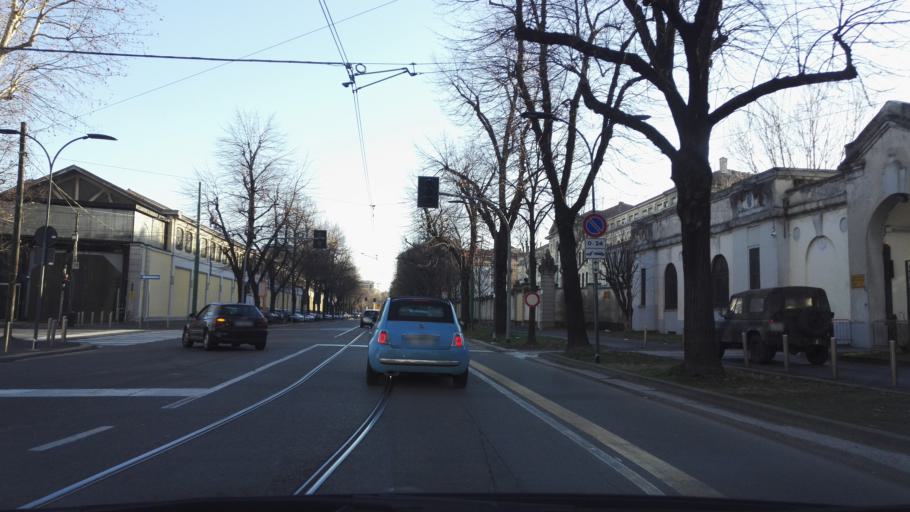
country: IT
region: Lombardy
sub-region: Citta metropolitana di Milano
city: Romano Banco
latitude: 45.4653
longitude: 9.1272
